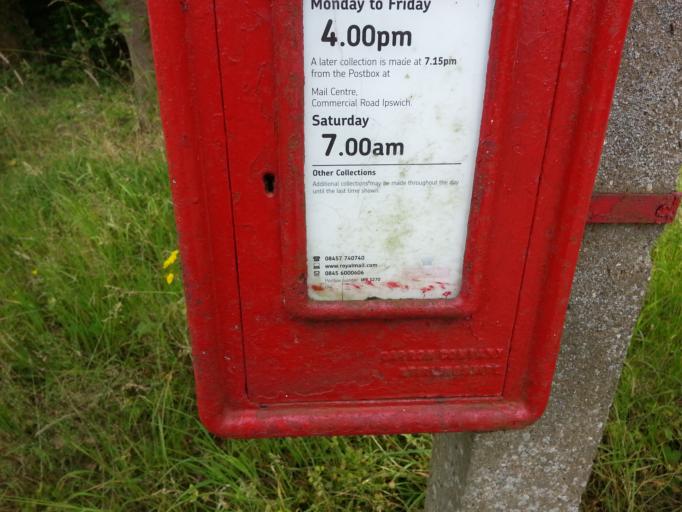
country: GB
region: England
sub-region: Suffolk
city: Ipswich
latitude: 51.9715
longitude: 1.1683
